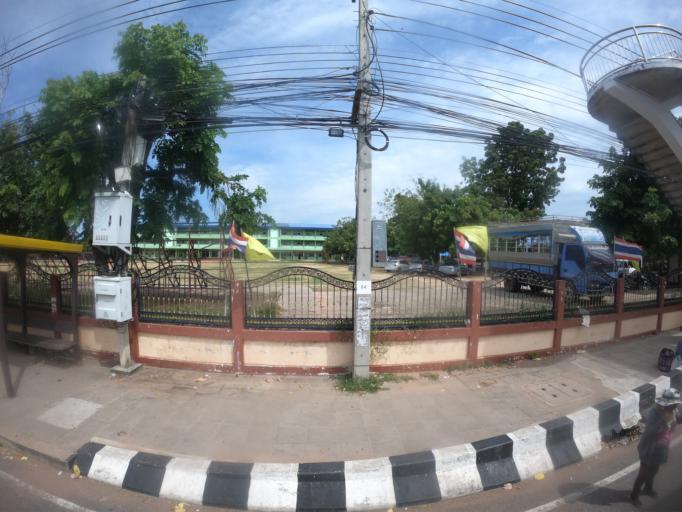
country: TH
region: Maha Sarakham
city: Chiang Yuen
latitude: 16.4111
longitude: 103.0952
